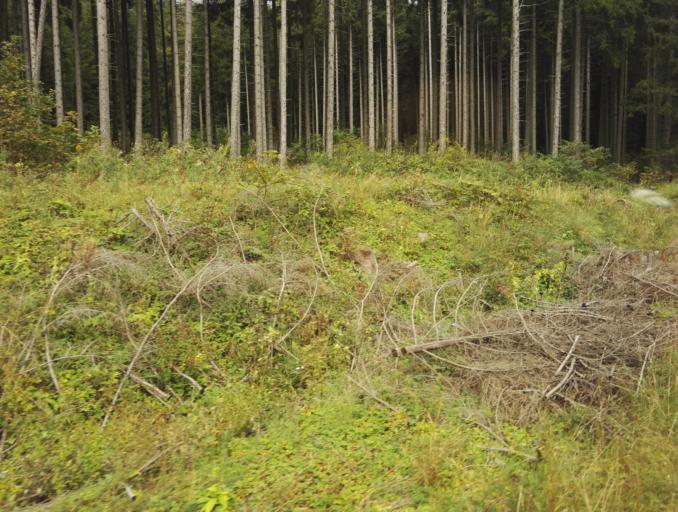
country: AT
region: Styria
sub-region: Politischer Bezirk Leoben
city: Vordernberg
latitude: 47.5116
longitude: 14.9784
